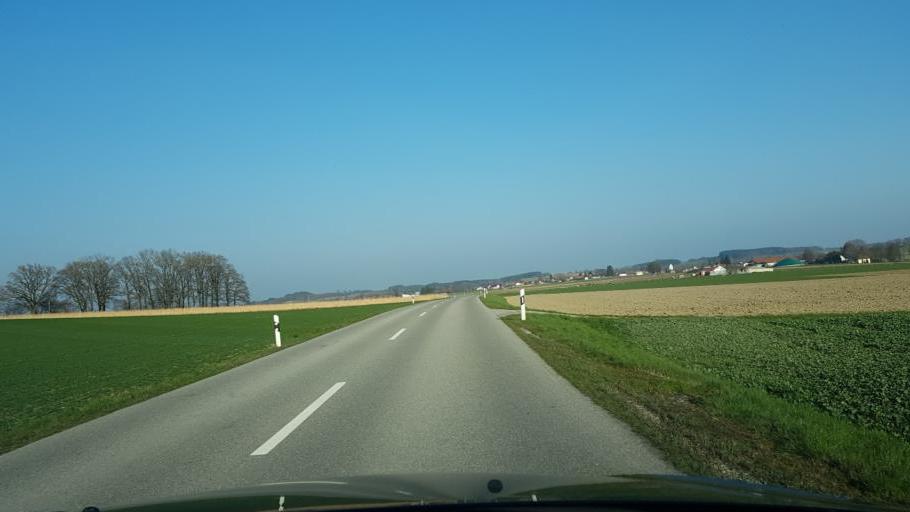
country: DE
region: Bavaria
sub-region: Upper Bavaria
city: Oberschweinbach
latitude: 48.2555
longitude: 11.1575
